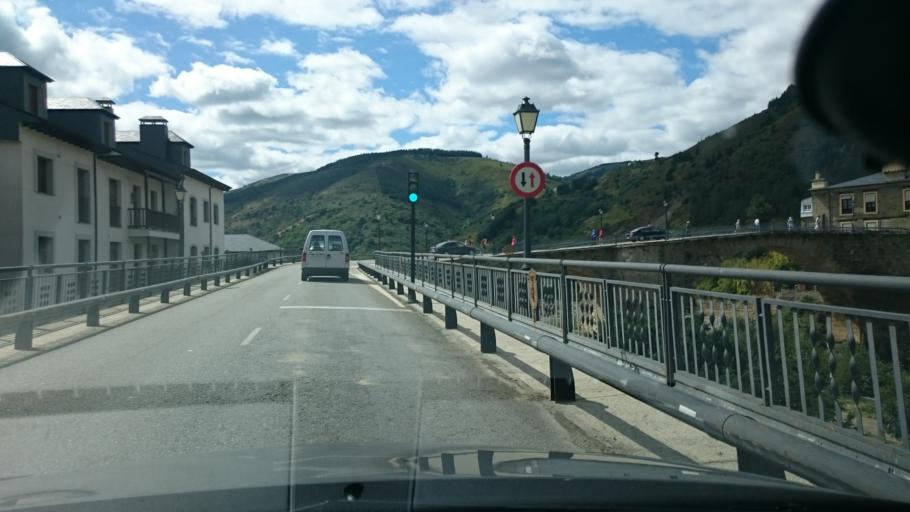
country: ES
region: Castille and Leon
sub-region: Provincia de Leon
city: Villafranca del Bierzo
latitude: 42.6094
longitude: -6.8108
